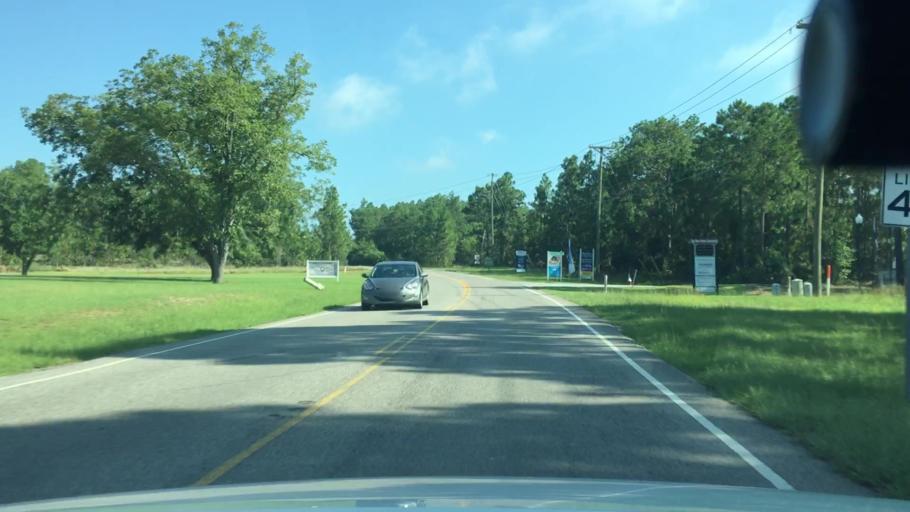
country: US
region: South Carolina
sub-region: Aiken County
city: Graniteville
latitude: 33.5909
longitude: -81.8366
